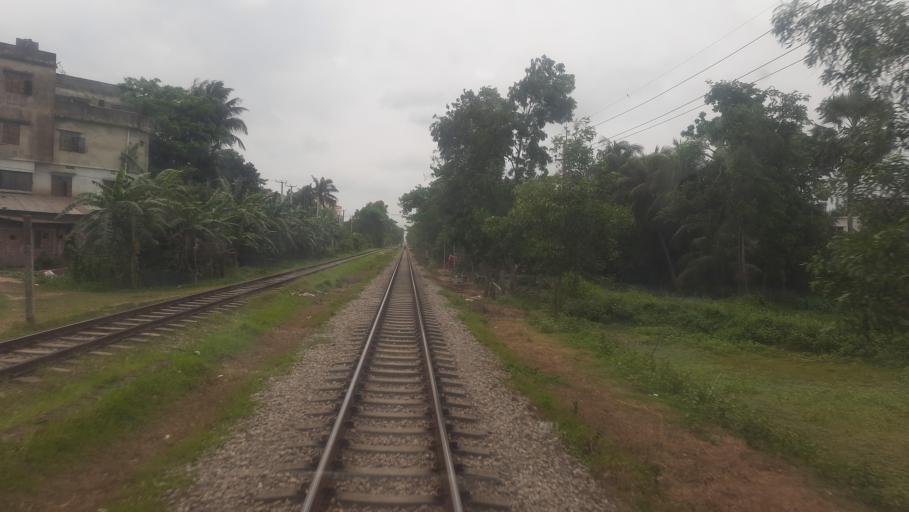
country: BD
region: Chittagong
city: Feni
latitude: 23.0258
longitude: 91.3859
